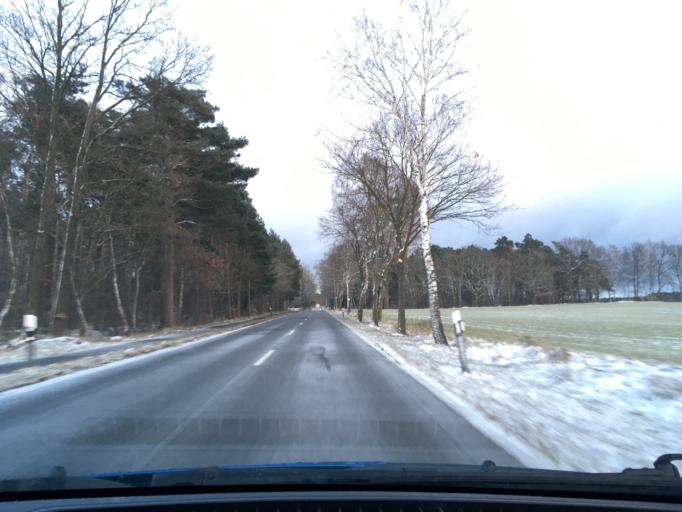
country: DE
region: Lower Saxony
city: Kirchgellersen
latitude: 53.2252
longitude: 10.3169
